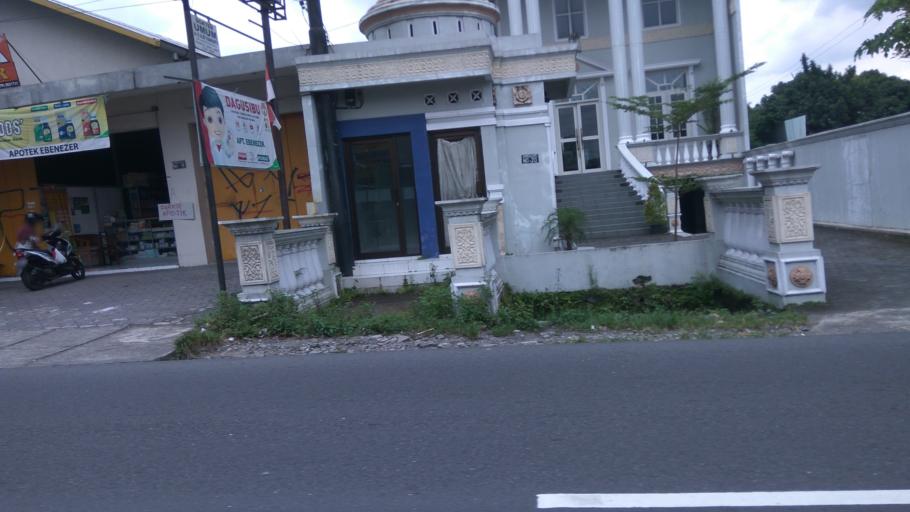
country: ID
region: Daerah Istimewa Yogyakarta
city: Melati
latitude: -7.7338
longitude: 110.3779
